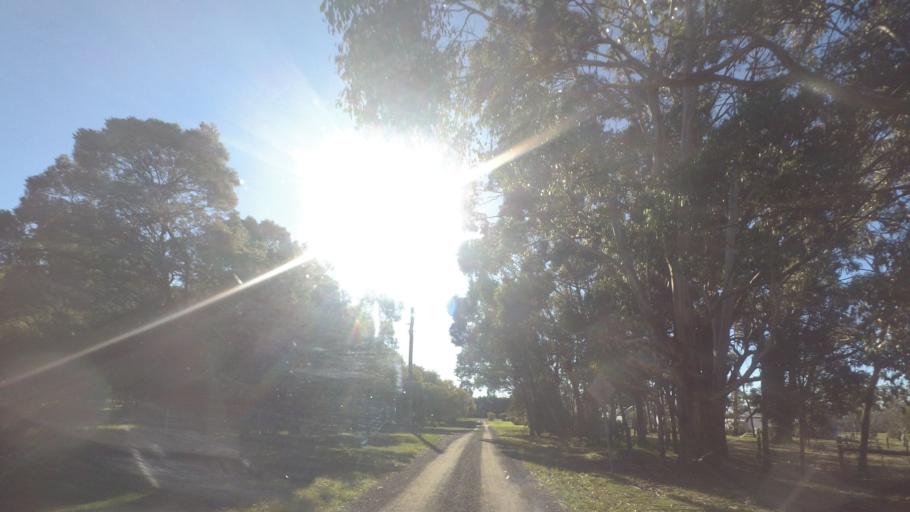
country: AU
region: Victoria
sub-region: Mount Alexander
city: Castlemaine
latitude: -37.3029
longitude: 144.3350
